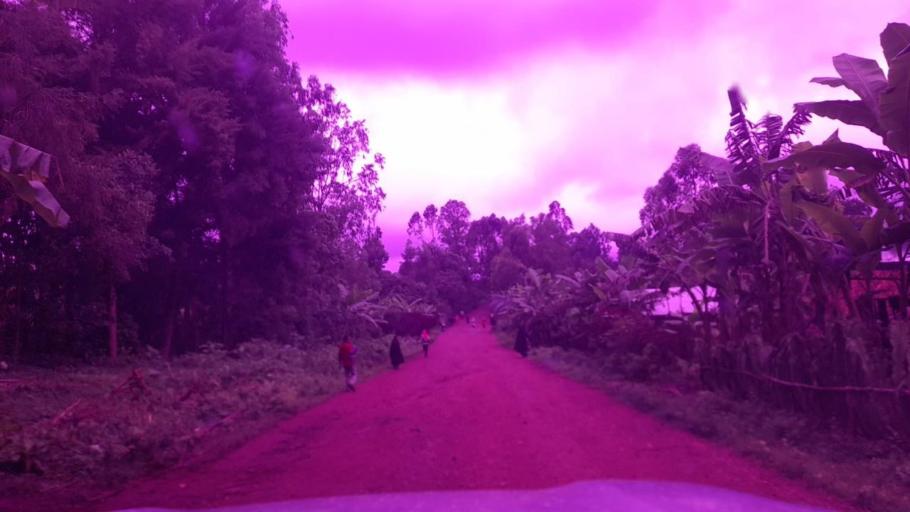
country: ET
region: Southern Nations, Nationalities, and People's Region
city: Bonga
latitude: 7.5842
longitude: 36.0175
